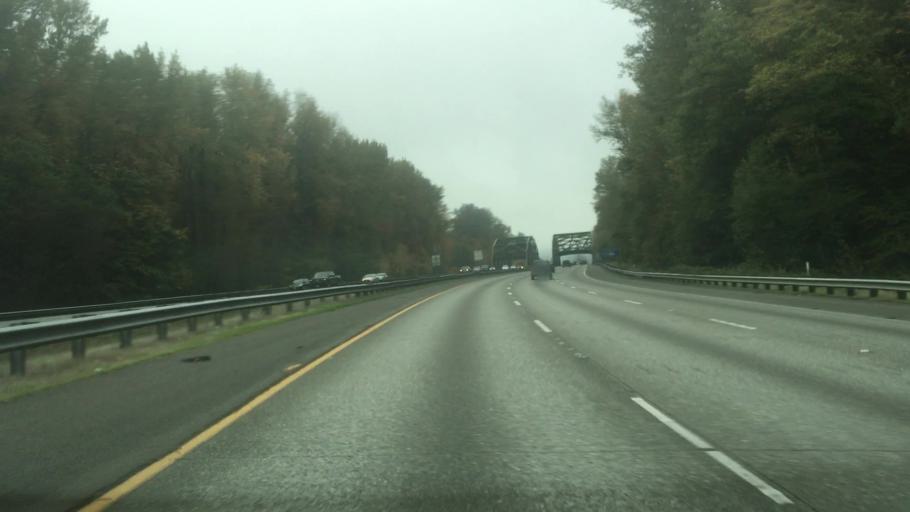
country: US
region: Washington
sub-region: Pierce County
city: DuPont
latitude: 47.0736
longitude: -122.6996
